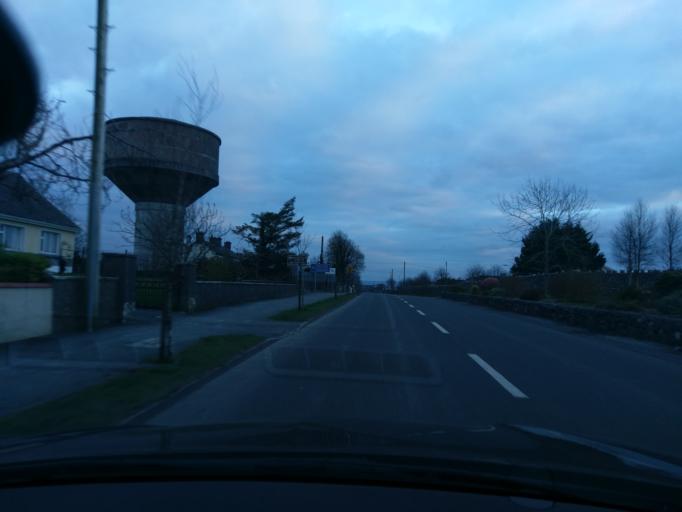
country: IE
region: Connaught
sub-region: County Galway
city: Athenry
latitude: 53.3063
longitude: -8.7516
